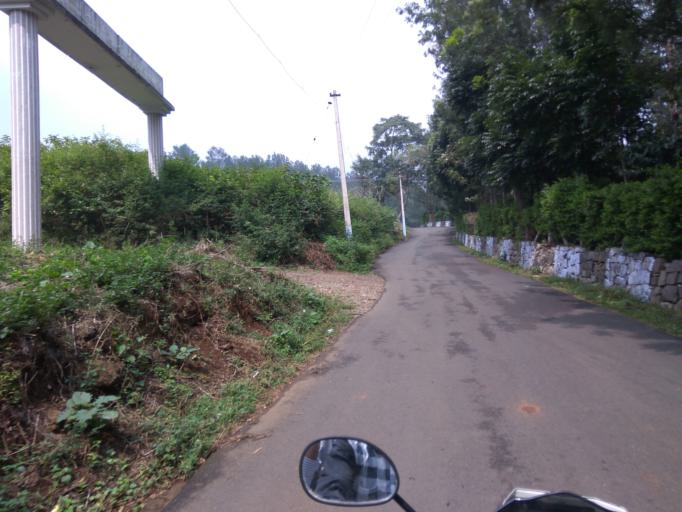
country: IN
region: Tamil Nadu
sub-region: Salem
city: Salem
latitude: 11.7718
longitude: 78.2336
